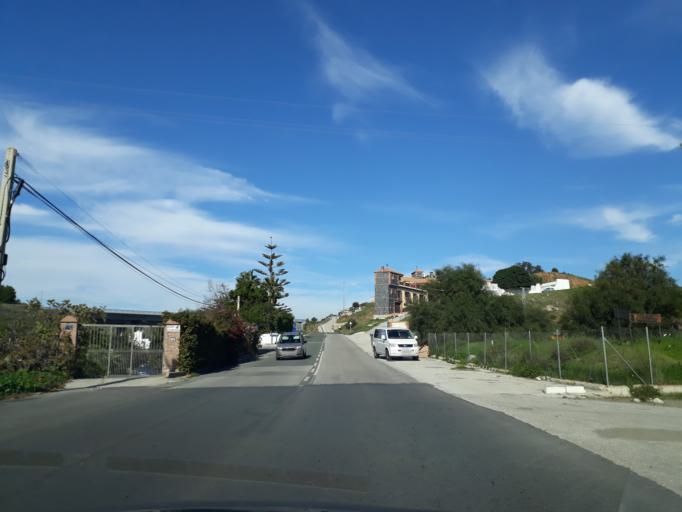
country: ES
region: Andalusia
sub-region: Provincia de Malaga
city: Fuengirola
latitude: 36.5201
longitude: -4.6845
